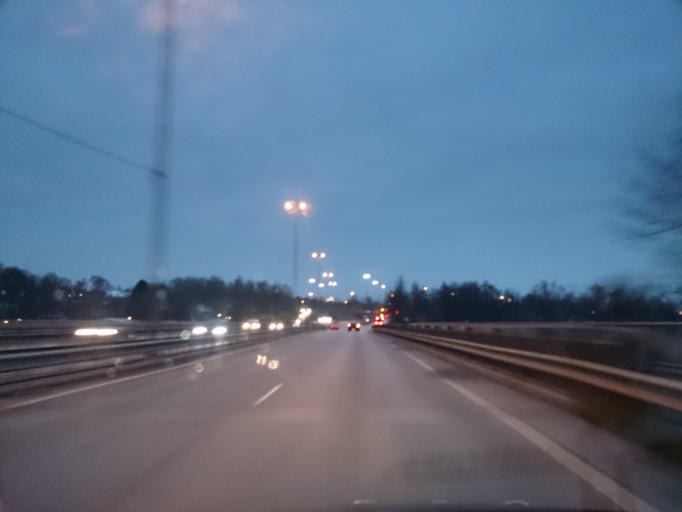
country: SE
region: OEstergoetland
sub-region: Norrkopings Kommun
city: Norrkoping
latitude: 58.5882
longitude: 16.1514
